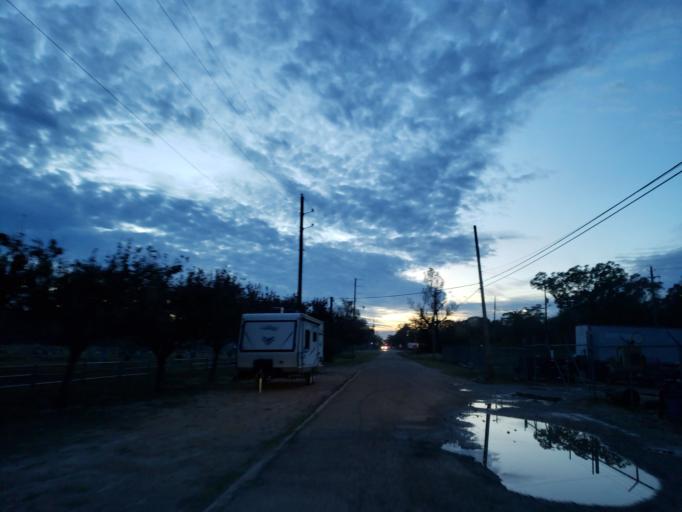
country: US
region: Mississippi
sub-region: Forrest County
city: Hattiesburg
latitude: 31.3251
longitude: -89.2687
